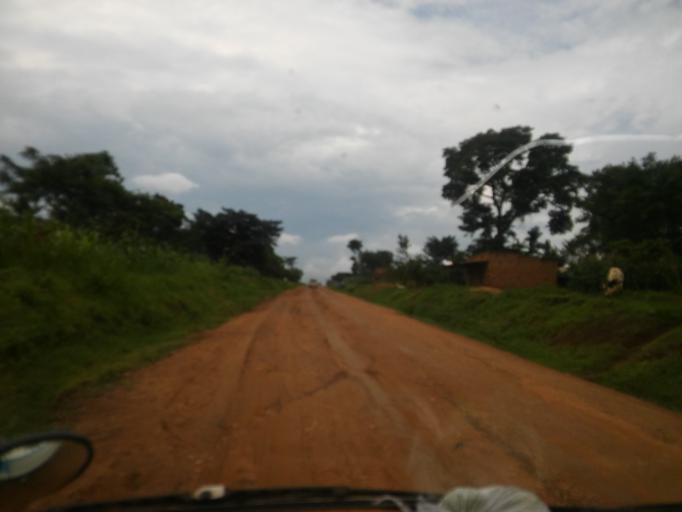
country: UG
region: Eastern Region
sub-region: Bududa District
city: Bududa
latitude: 0.9490
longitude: 34.2493
